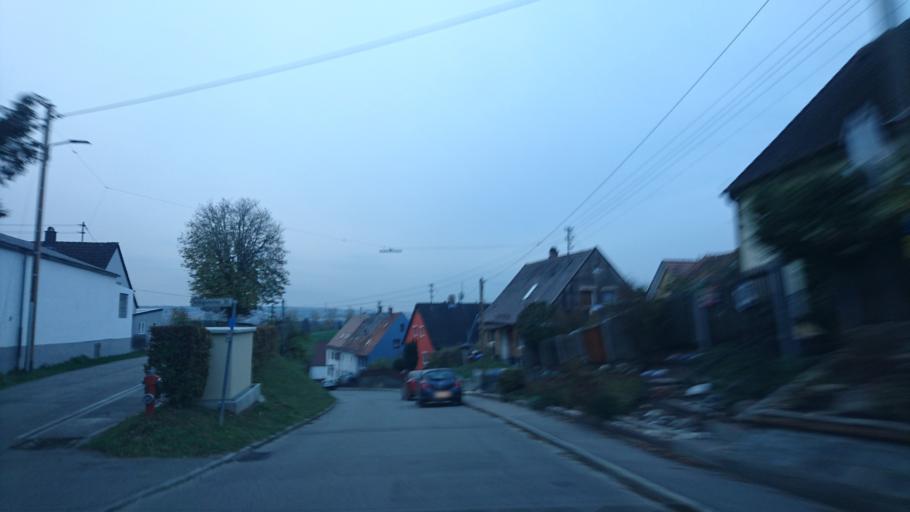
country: DE
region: Bavaria
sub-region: Swabia
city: Diedorf
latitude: 48.3765
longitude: 10.7850
